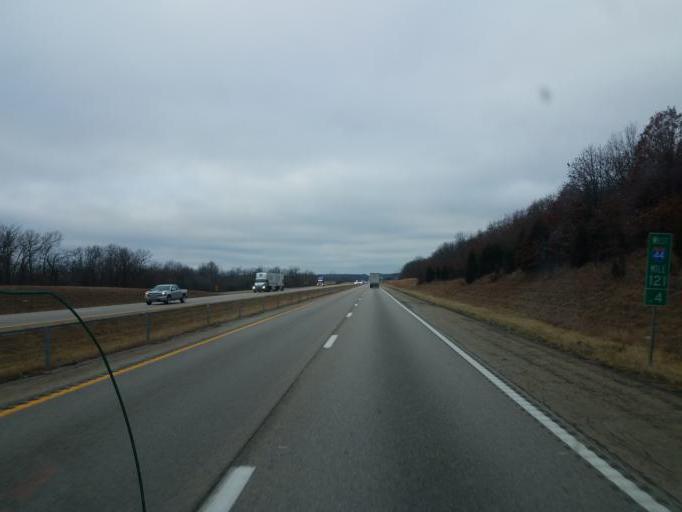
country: US
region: Missouri
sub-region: Laclede County
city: Lebanon
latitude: 37.5859
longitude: -92.7407
